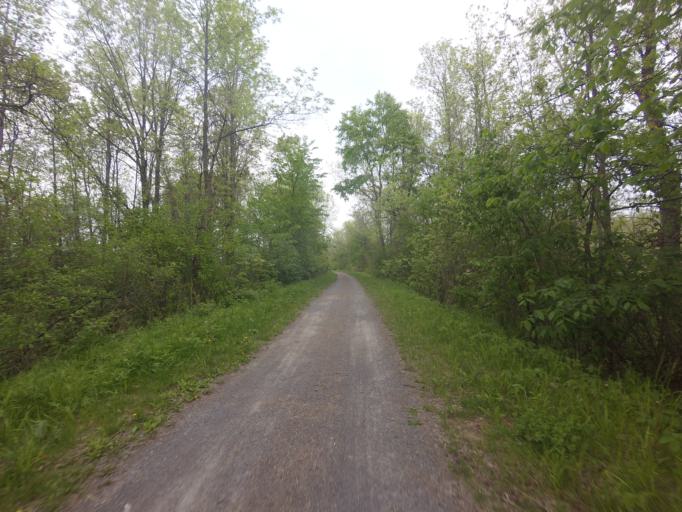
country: CA
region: Ontario
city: Kingston
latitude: 44.2890
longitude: -76.5592
